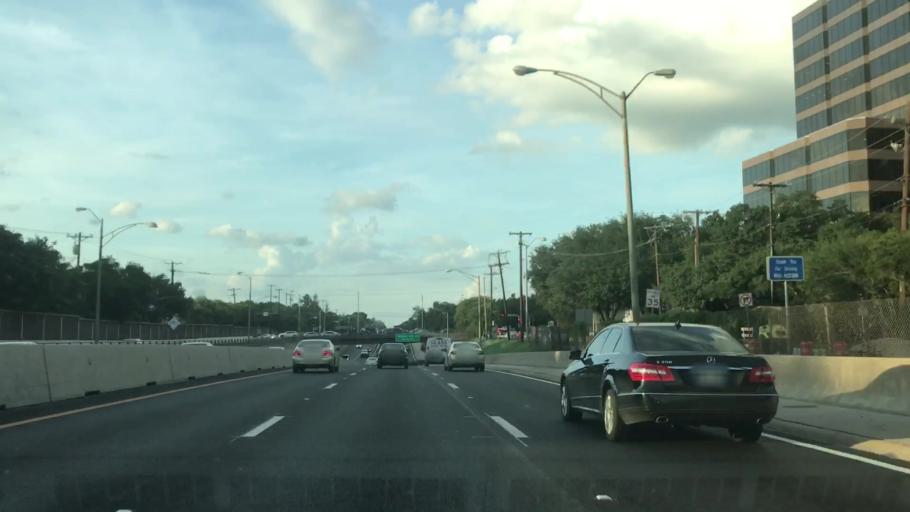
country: US
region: Texas
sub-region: Dallas County
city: University Park
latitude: 32.8637
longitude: -96.8116
